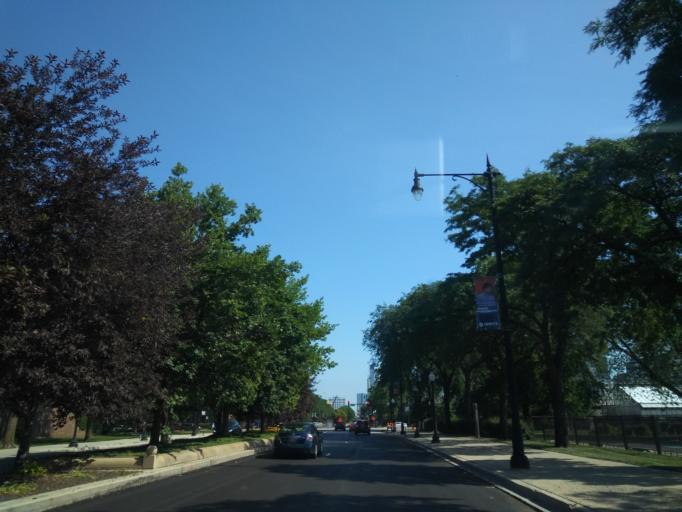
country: US
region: Illinois
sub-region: Cook County
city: Chicago
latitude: 41.8685
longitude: -87.6468
